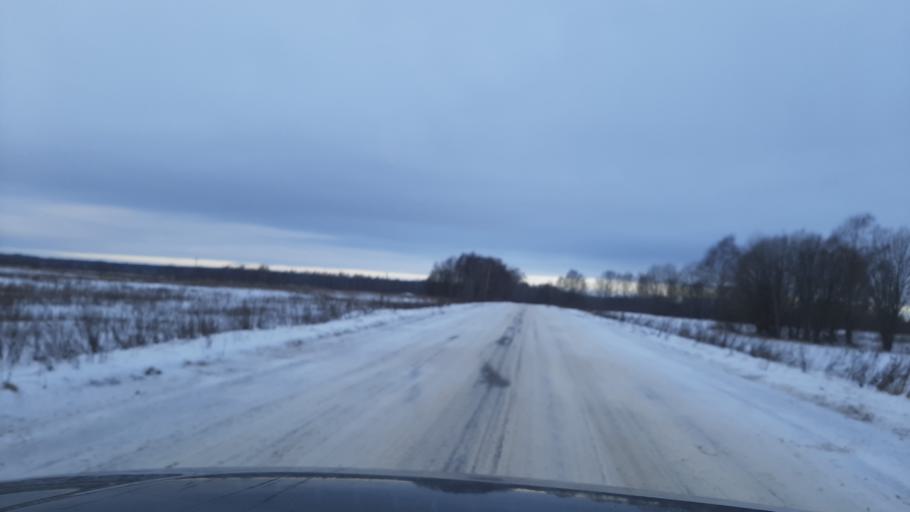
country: RU
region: Kostroma
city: Volgorechensk
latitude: 57.4365
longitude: 41.0556
